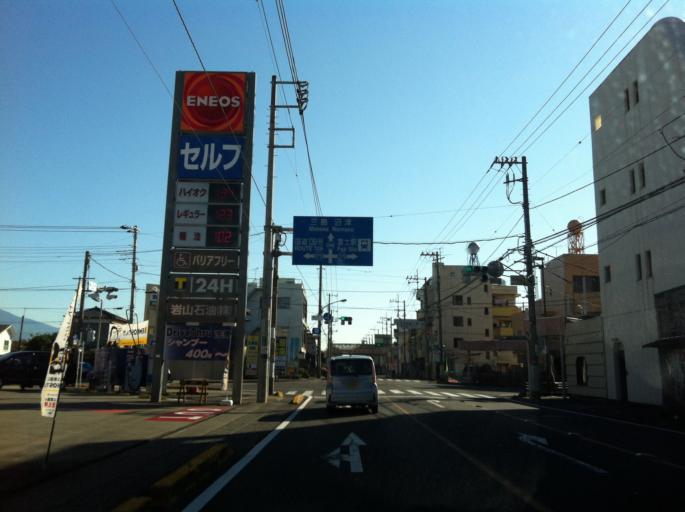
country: JP
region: Shizuoka
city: Fuji
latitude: 35.1576
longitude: 138.6514
